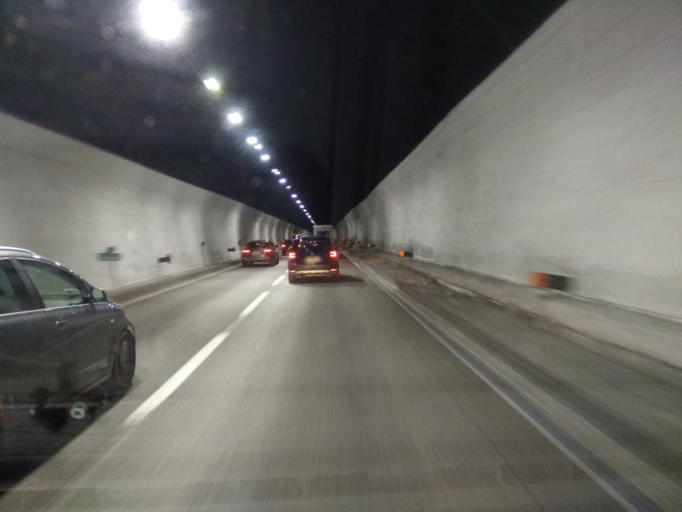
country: IT
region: Tuscany
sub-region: Province of Florence
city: Cavallina
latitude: 43.9417
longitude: 11.2205
